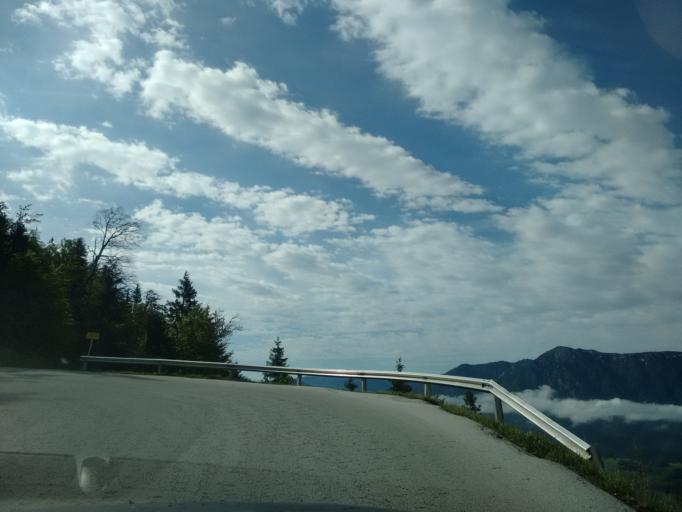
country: AT
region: Styria
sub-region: Politischer Bezirk Liezen
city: Altaussee
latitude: 47.6531
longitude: 13.7630
